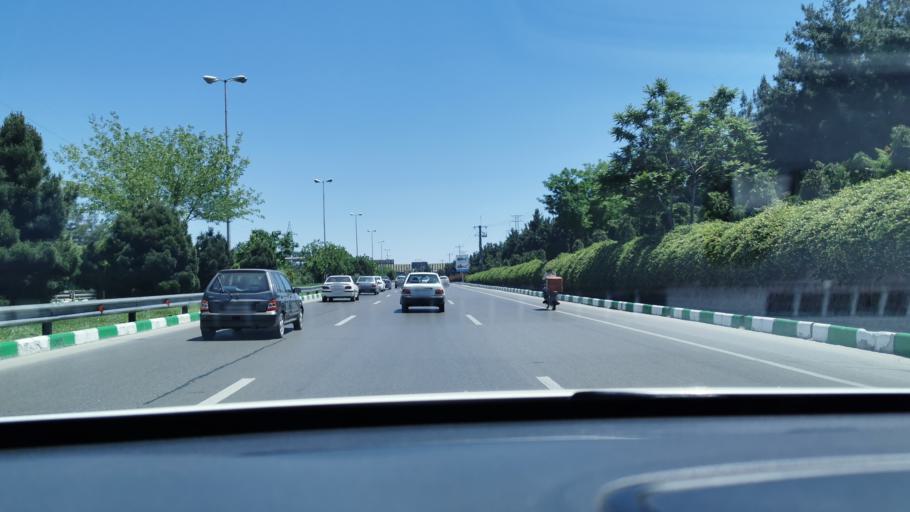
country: IR
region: Razavi Khorasan
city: Mashhad
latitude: 36.2607
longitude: 59.5853
